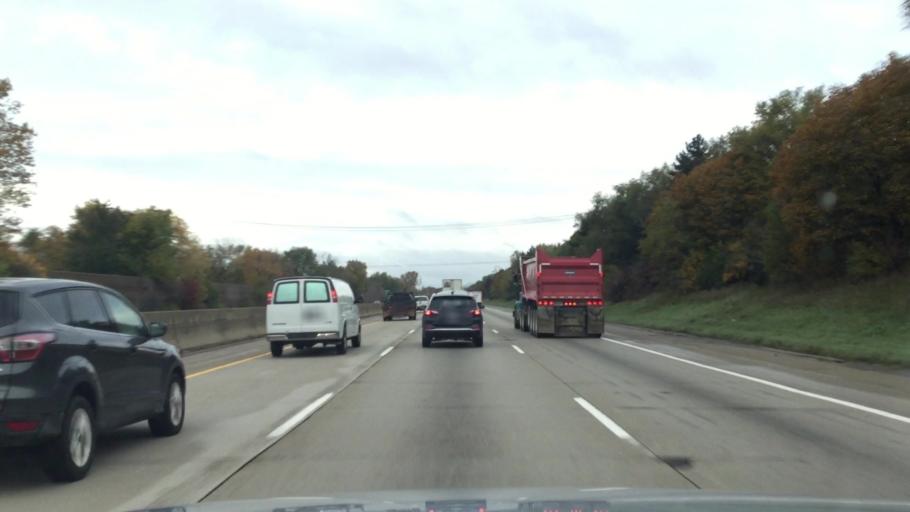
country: US
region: Michigan
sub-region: Washtenaw County
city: Ypsilanti
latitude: 42.2240
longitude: -83.5674
